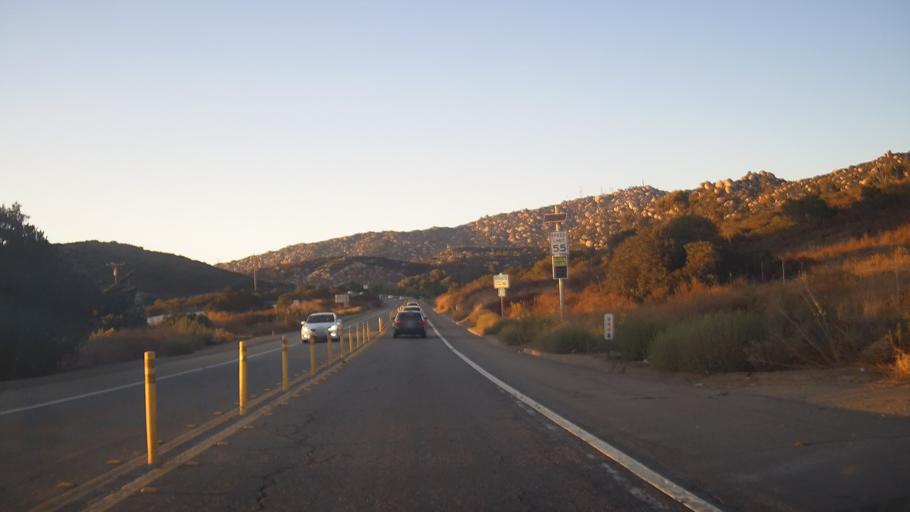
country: US
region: California
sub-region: San Diego County
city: Poway
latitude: 32.9841
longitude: -116.9742
